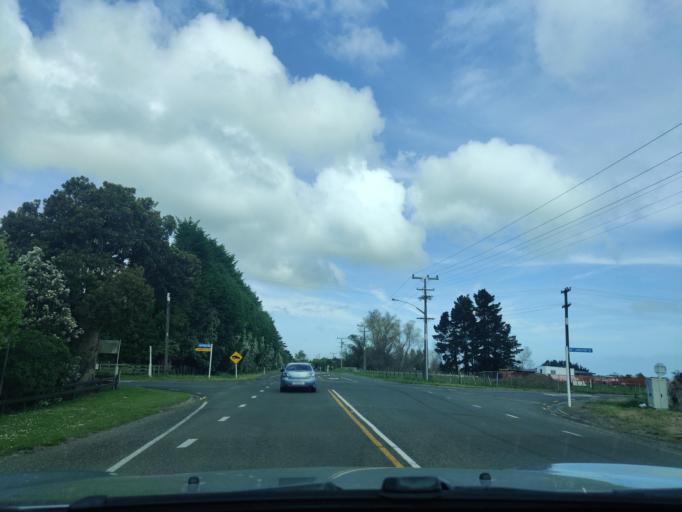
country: NZ
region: Manawatu-Wanganui
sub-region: Wanganui District
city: Wanganui
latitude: -39.8760
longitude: 174.9980
